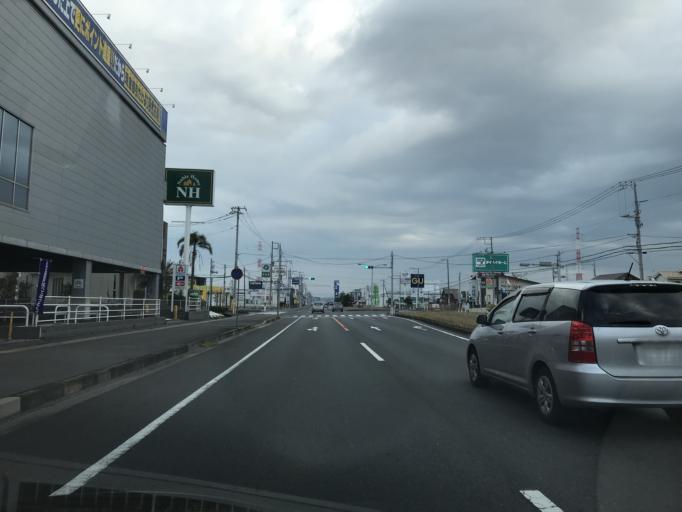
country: JP
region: Ibaraki
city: Kashima-shi
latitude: 35.9180
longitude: 140.6377
